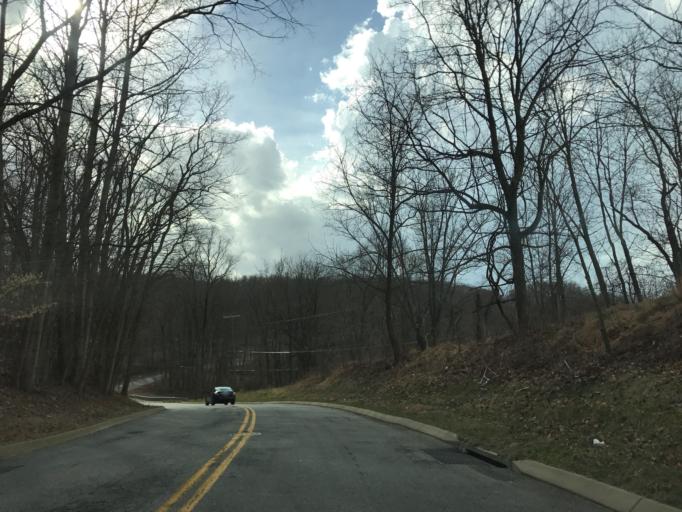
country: US
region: Maryland
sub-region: Harford County
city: South Bel Air
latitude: 39.5783
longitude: -76.3098
